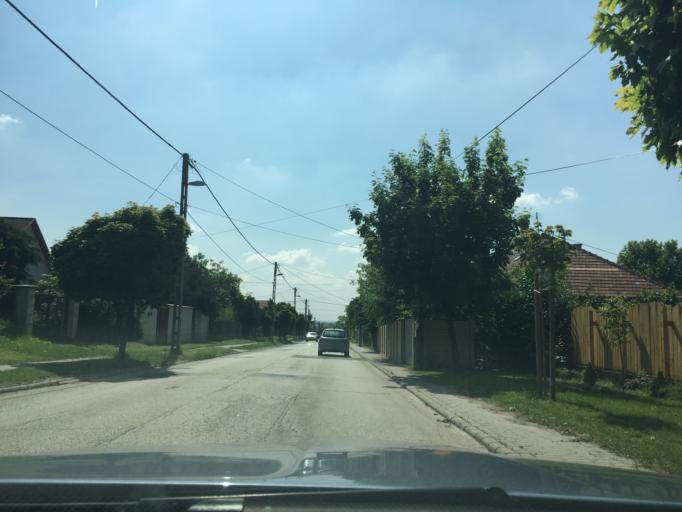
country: HU
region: Budapest
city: Budapest XXII. keruelet
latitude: 47.4168
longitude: 19.0189
